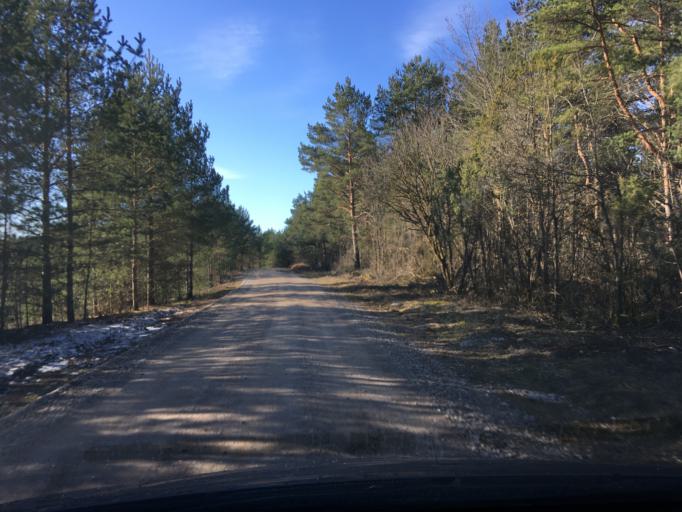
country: EE
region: Laeaene
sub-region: Lihula vald
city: Lihula
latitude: 58.5792
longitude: 23.7028
